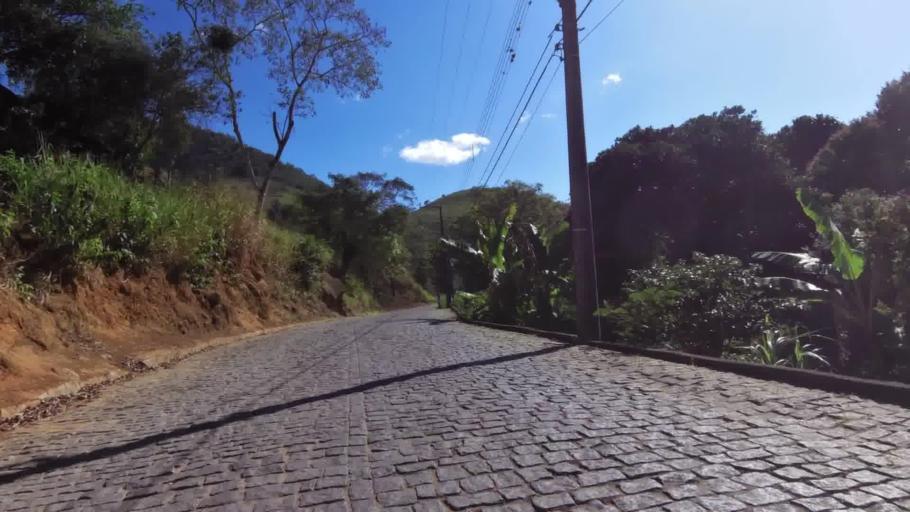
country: BR
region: Espirito Santo
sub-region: Rio Novo Do Sul
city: Rio Novo do Sul
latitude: -20.8580
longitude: -40.9316
